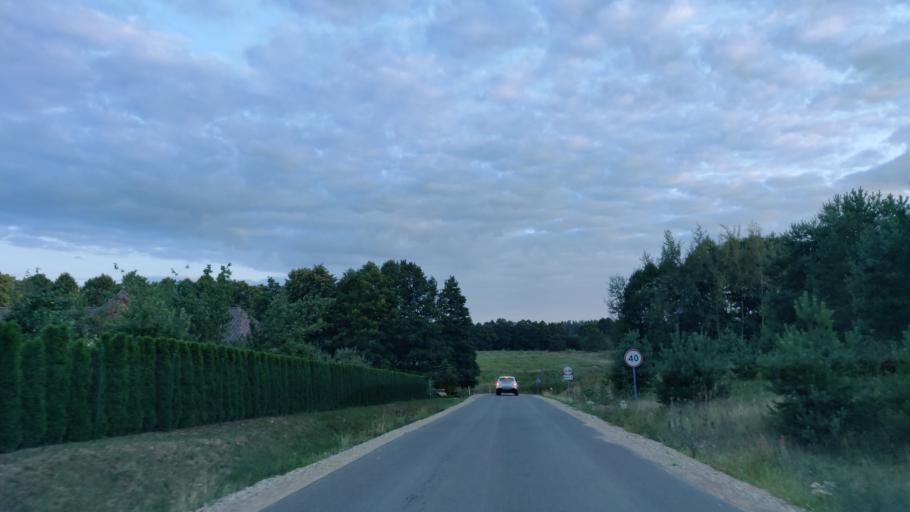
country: LT
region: Vilnius County
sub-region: Trakai
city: Rudiskes
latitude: 54.6104
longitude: 24.8184
